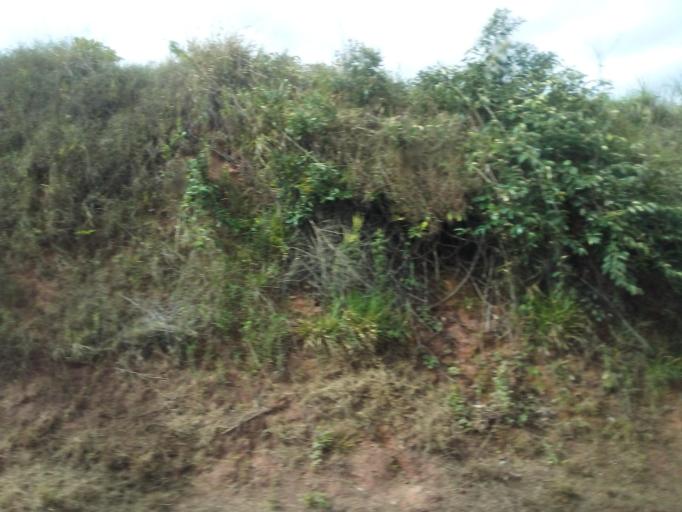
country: BR
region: Minas Gerais
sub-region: Caete
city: Caete
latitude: -19.9073
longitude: -43.7173
